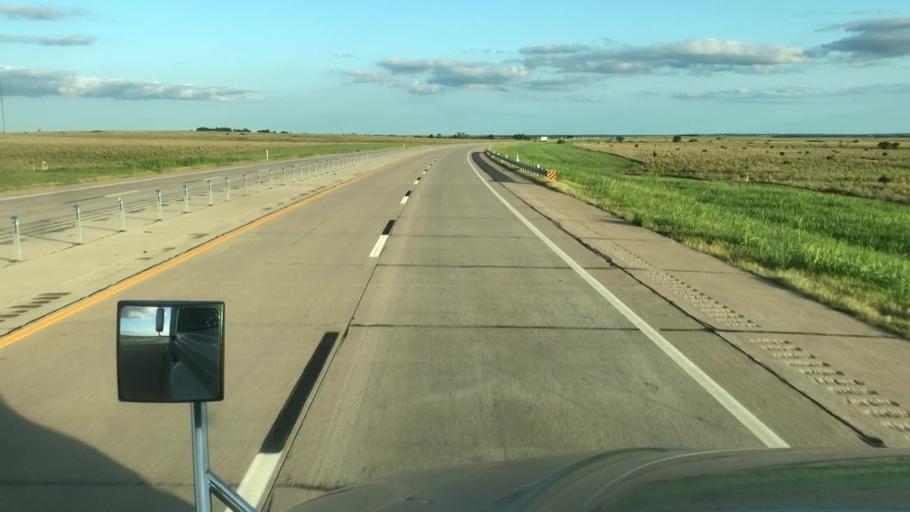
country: US
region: Oklahoma
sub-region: Pawnee County
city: Pawnee
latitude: 36.3711
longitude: -97.0377
